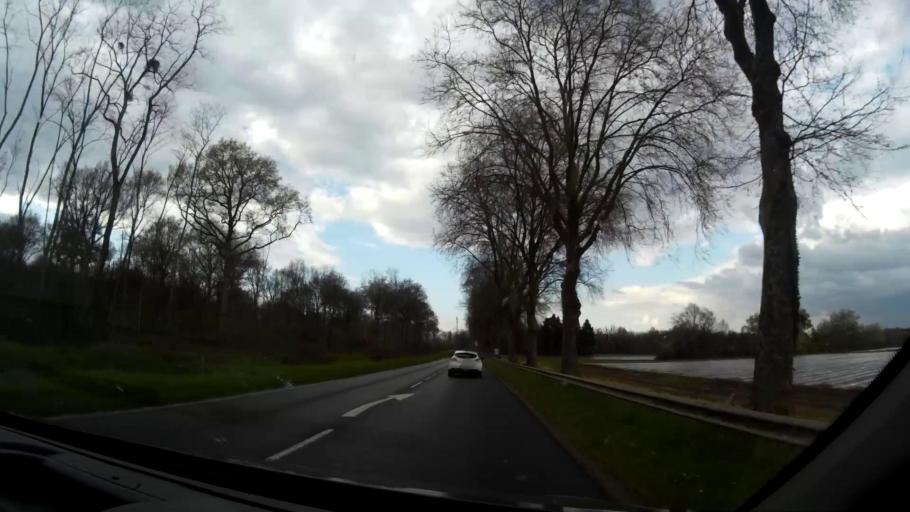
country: FR
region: Centre
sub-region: Departement du Loir-et-Cher
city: Cormeray
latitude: 47.4663
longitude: 1.4246
